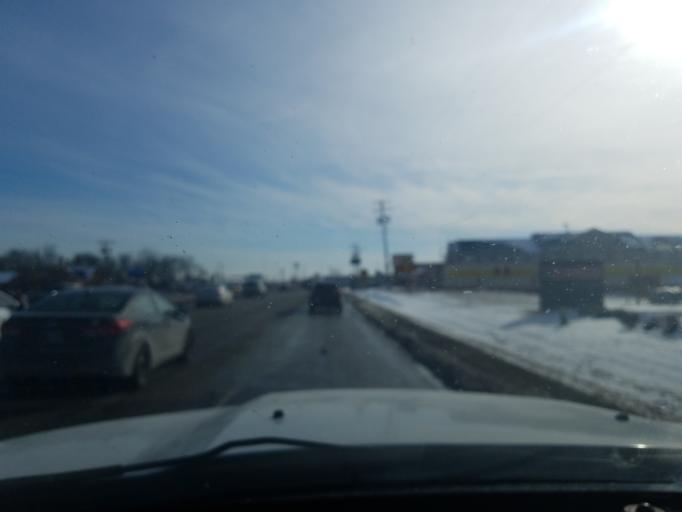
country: US
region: Indiana
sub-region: Allen County
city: Fort Wayne
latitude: 41.1354
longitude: -85.1615
